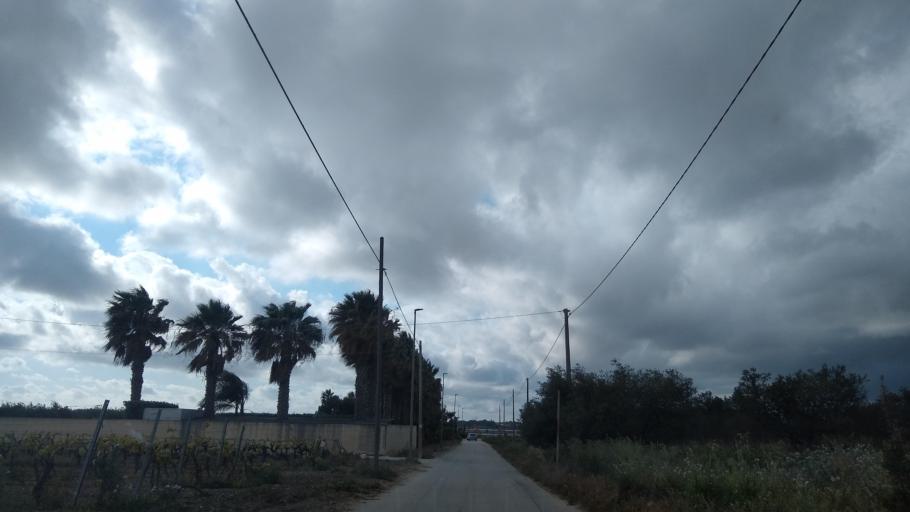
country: IT
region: Sicily
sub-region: Trapani
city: Marsala
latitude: 37.8562
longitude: 12.4860
